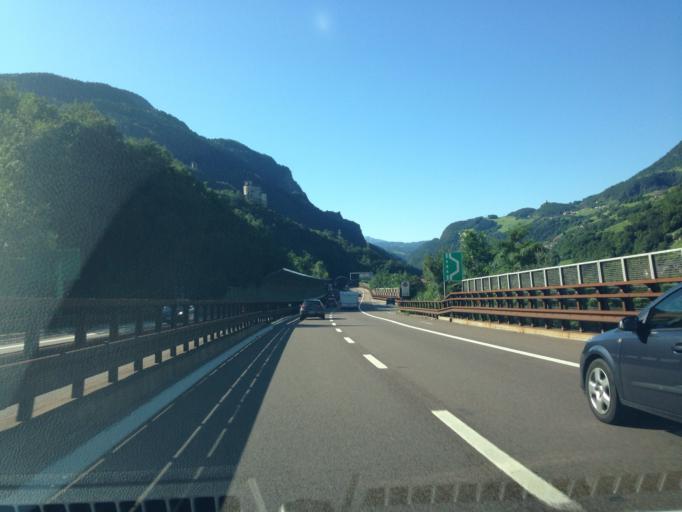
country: IT
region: Trentino-Alto Adige
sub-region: Bolzano
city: Ponte Gardena
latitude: 46.6039
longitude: 11.5349
